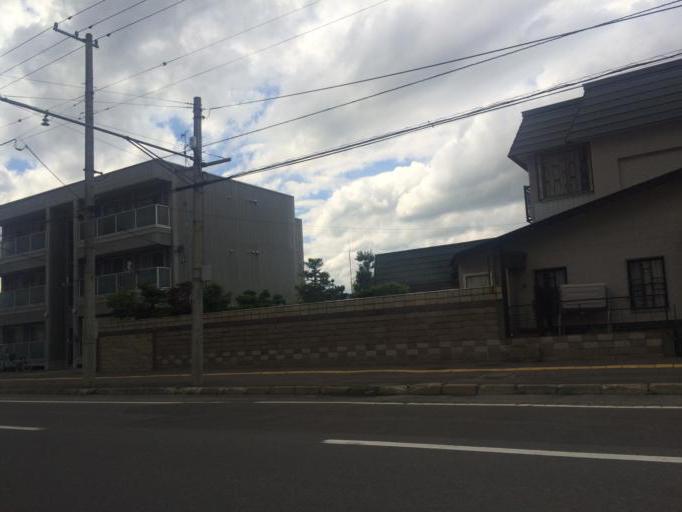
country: JP
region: Hokkaido
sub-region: Asahikawa-shi
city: Asahikawa
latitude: 43.7587
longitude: 142.3348
